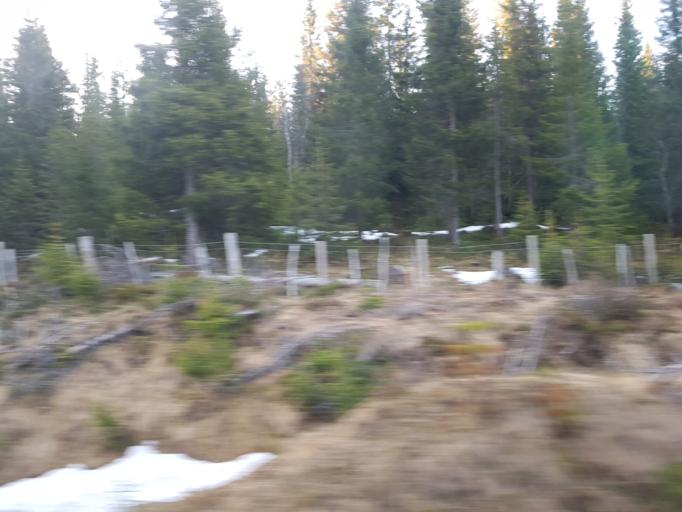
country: NO
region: Sor-Trondelag
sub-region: Rennebu
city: Berkak
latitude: 62.8677
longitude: 10.0302
